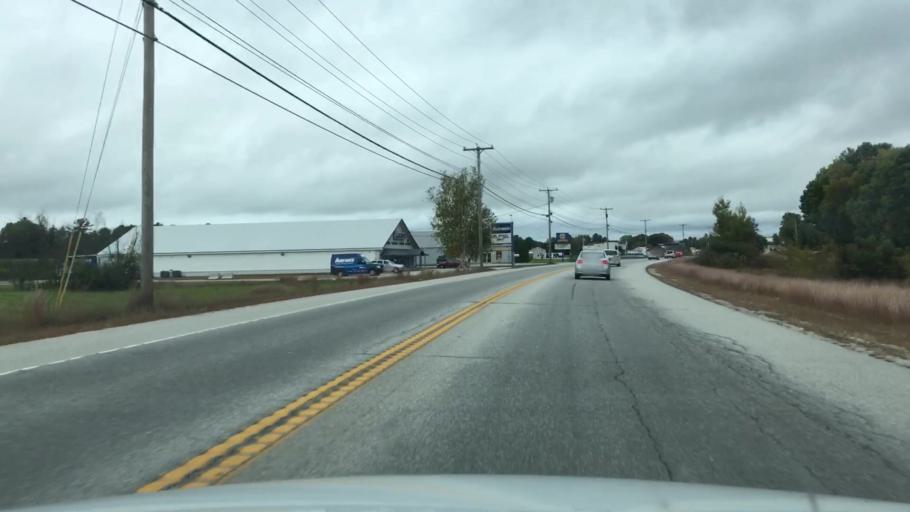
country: US
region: Maine
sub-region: Oxford County
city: South Paris
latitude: 44.1773
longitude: -70.5145
